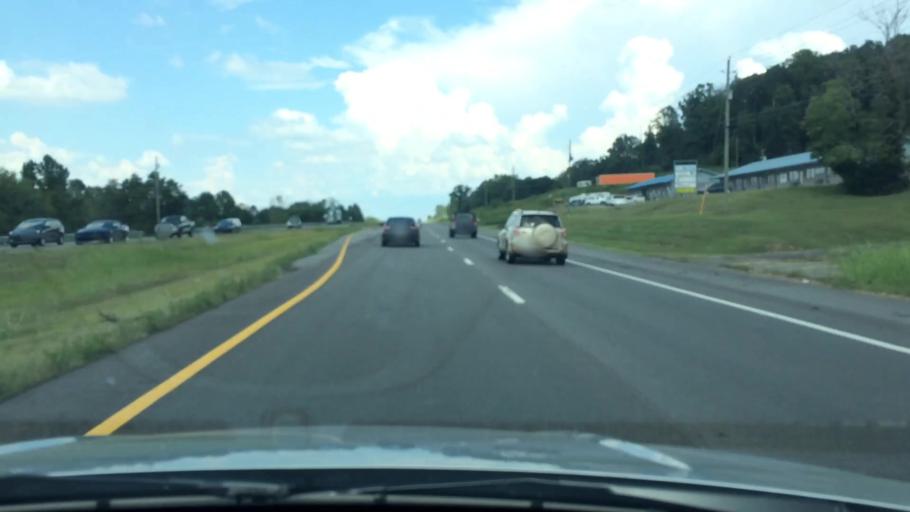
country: US
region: Tennessee
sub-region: Monroe County
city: Madisonville
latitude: 35.5535
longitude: -84.3088
